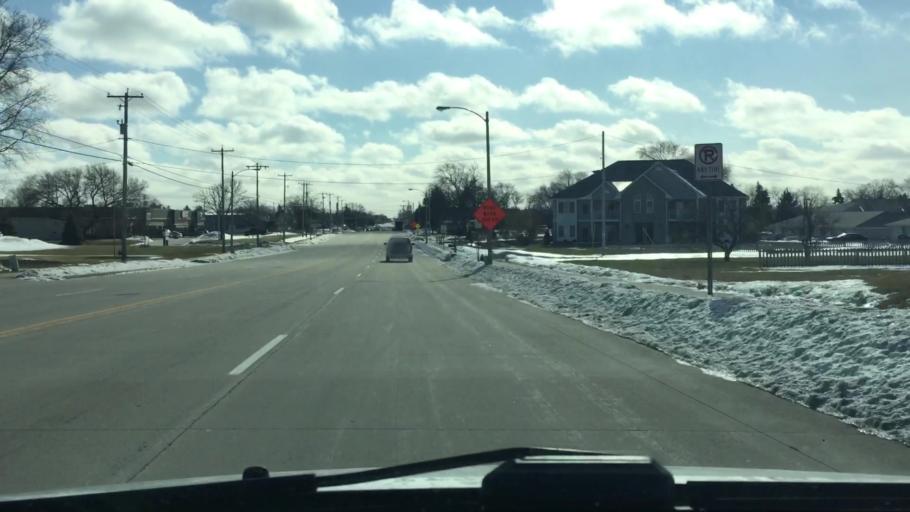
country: US
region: Wisconsin
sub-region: Milwaukee County
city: Greendale
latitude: 42.9202
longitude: -87.9307
